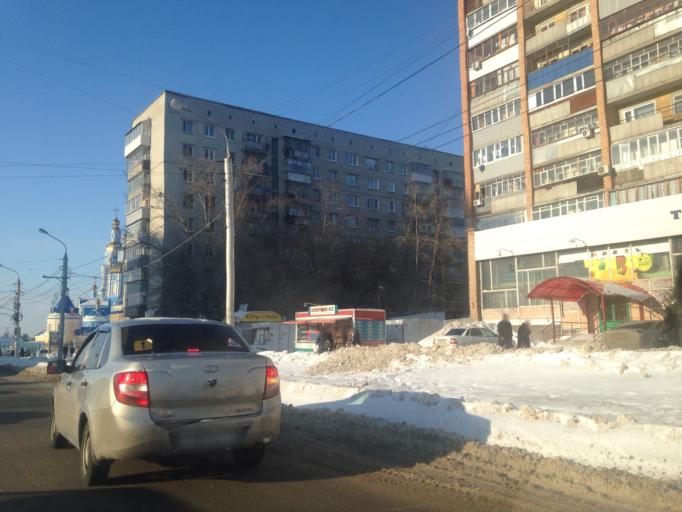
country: RU
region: Ulyanovsk
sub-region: Ulyanovskiy Rayon
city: Ulyanovsk
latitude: 54.3070
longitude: 48.3807
